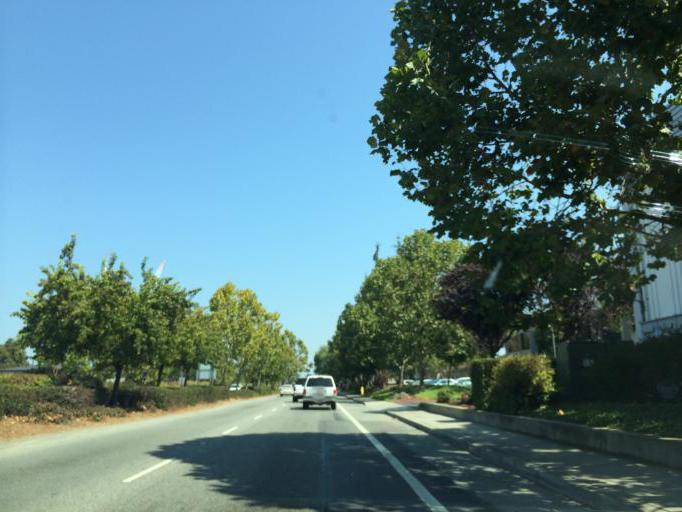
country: US
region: California
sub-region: San Mateo County
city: East Palo Alto
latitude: 37.4763
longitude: -122.1526
